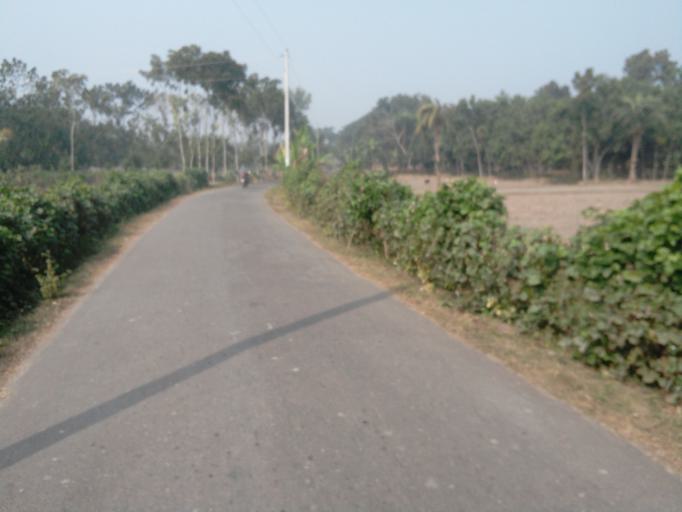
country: BD
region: Khulna
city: Kesabpur
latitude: 22.7500
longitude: 89.2409
